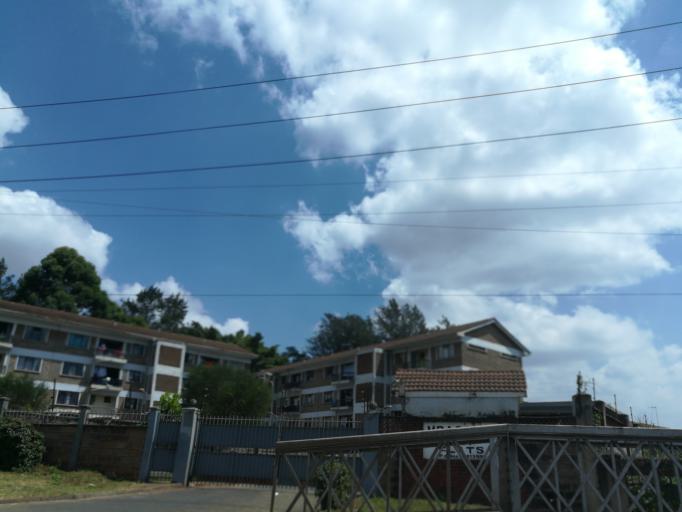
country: KE
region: Nairobi Area
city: Nairobi
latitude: -1.3005
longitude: 36.8028
